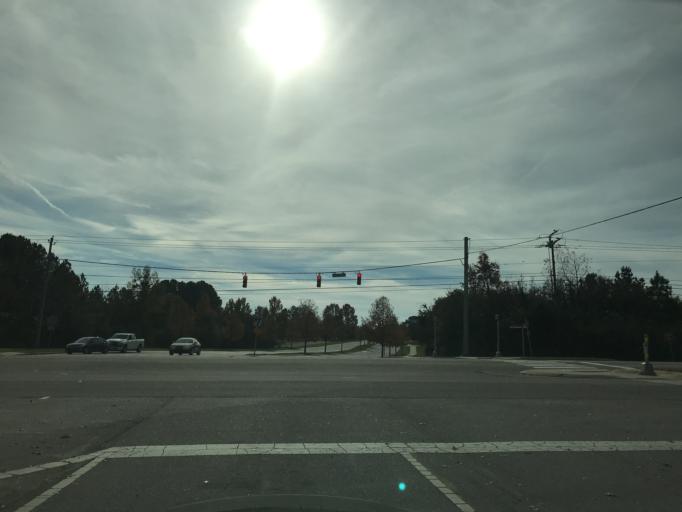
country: US
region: North Carolina
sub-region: Wake County
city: West Raleigh
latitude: 35.7840
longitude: -78.6823
